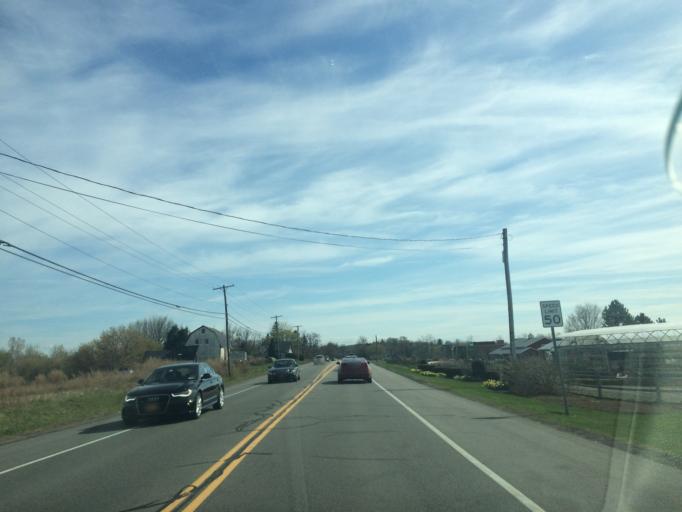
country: US
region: New York
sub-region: Monroe County
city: Fairport
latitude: 43.1524
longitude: -77.4340
